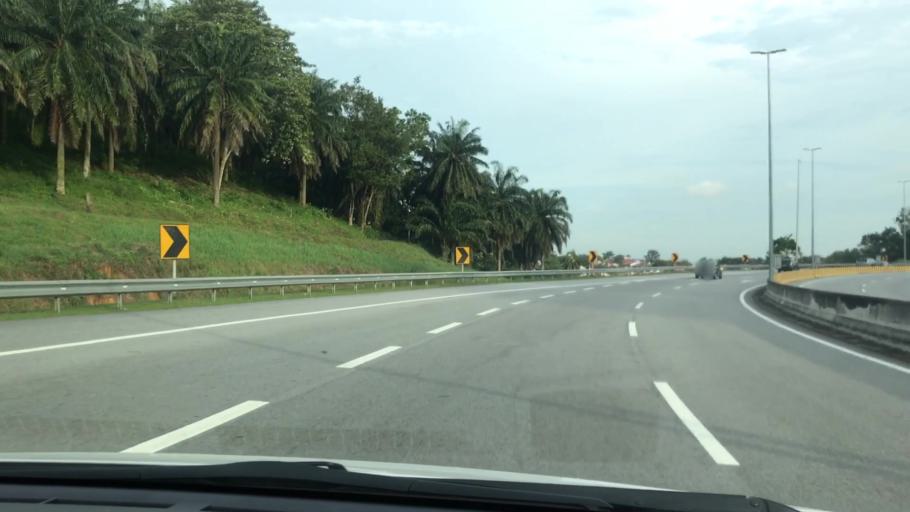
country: MY
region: Selangor
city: Kampong Baharu Balakong
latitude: 3.0123
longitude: 101.6863
